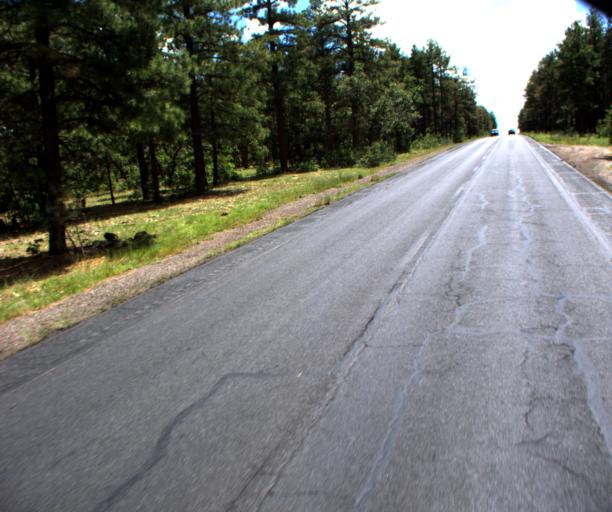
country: US
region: Arizona
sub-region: Gila County
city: Pine
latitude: 34.4920
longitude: -111.4578
